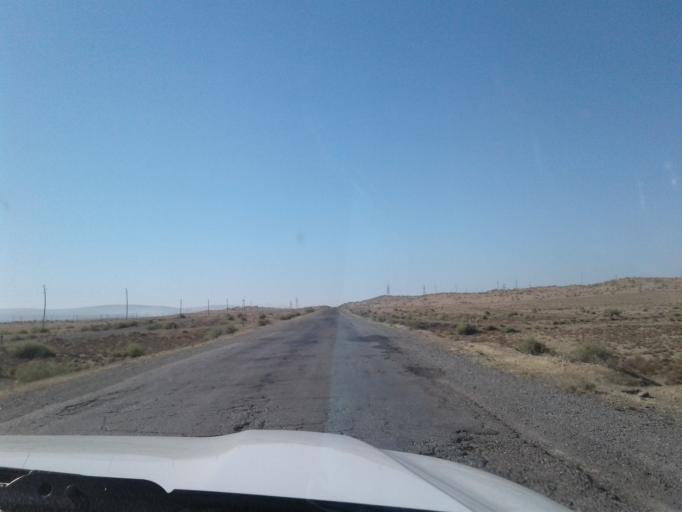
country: TM
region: Mary
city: Yoloeten
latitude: 36.5675
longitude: 62.5387
